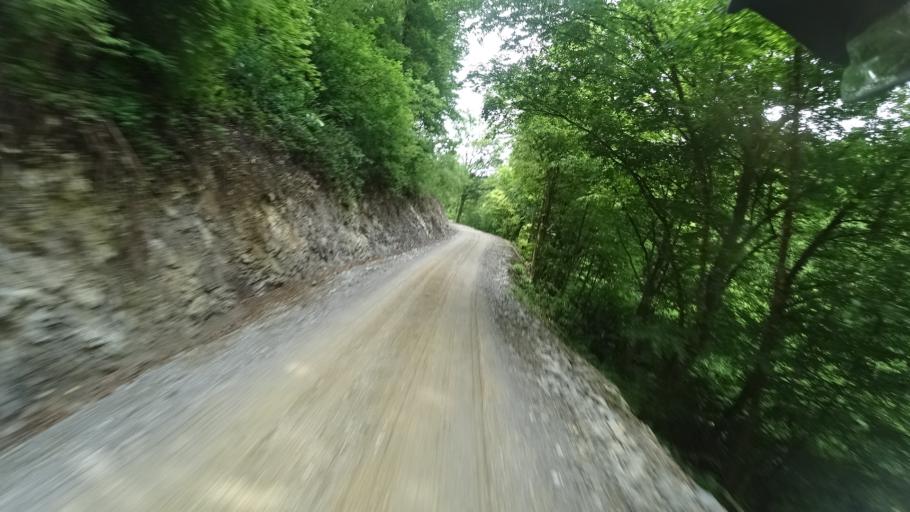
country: HR
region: Karlovacka
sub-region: Grad Karlovac
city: Slunj
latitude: 45.2132
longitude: 15.6336
